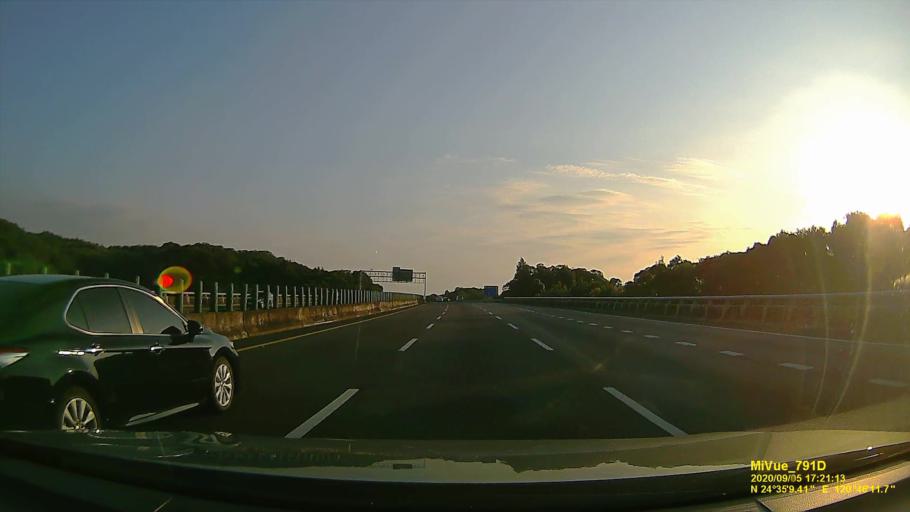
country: TW
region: Taiwan
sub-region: Miaoli
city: Miaoli
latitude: 24.5861
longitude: 120.7695
